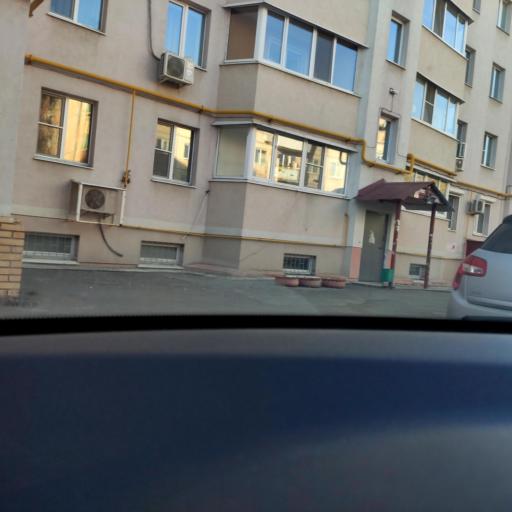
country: RU
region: Samara
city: Samara
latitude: 53.1909
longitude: 50.2022
